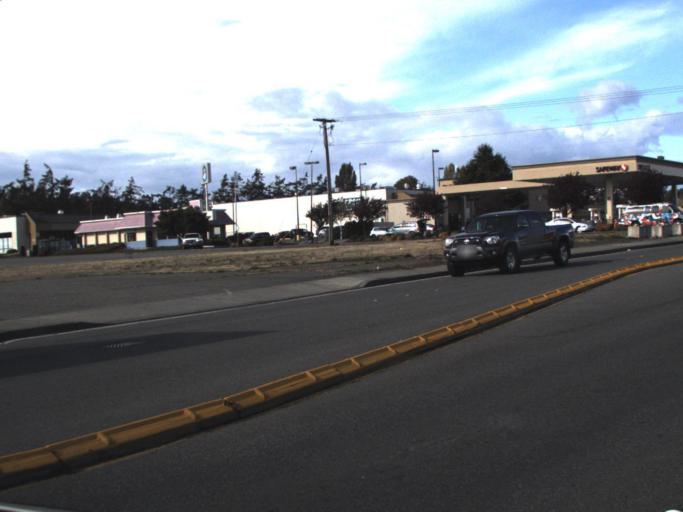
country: US
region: Washington
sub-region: Island County
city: Oak Harbor
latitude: 48.2878
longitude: -122.6578
